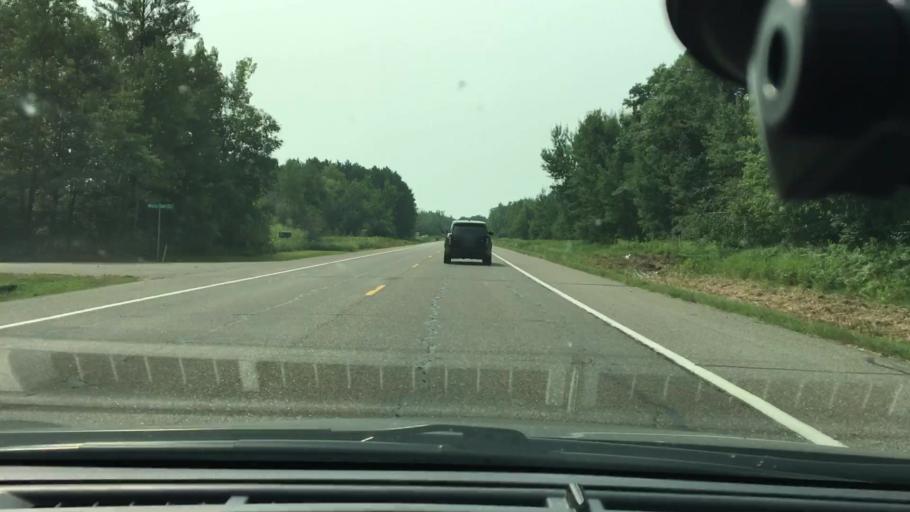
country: US
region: Minnesota
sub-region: Crow Wing County
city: Brainerd
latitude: 46.3914
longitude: -94.2233
